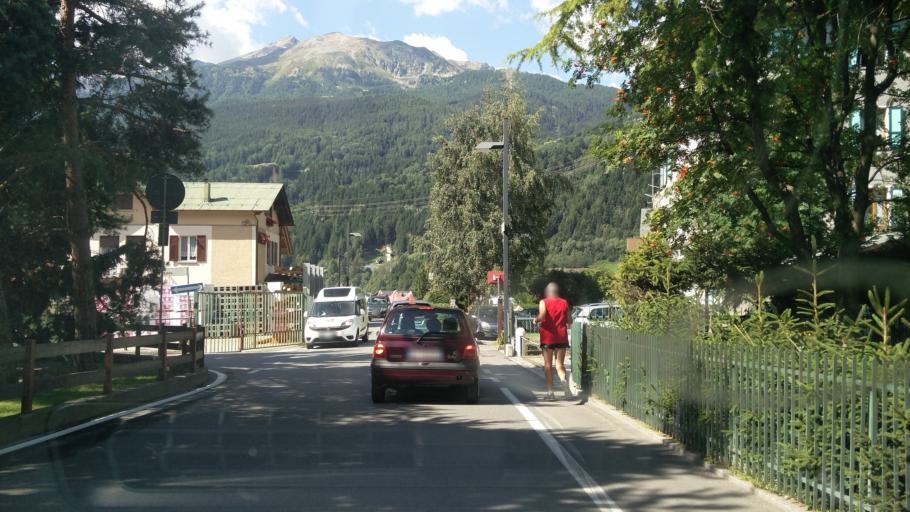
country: IT
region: Lombardy
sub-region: Provincia di Sondrio
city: Bormio
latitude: 46.4654
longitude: 10.3658
